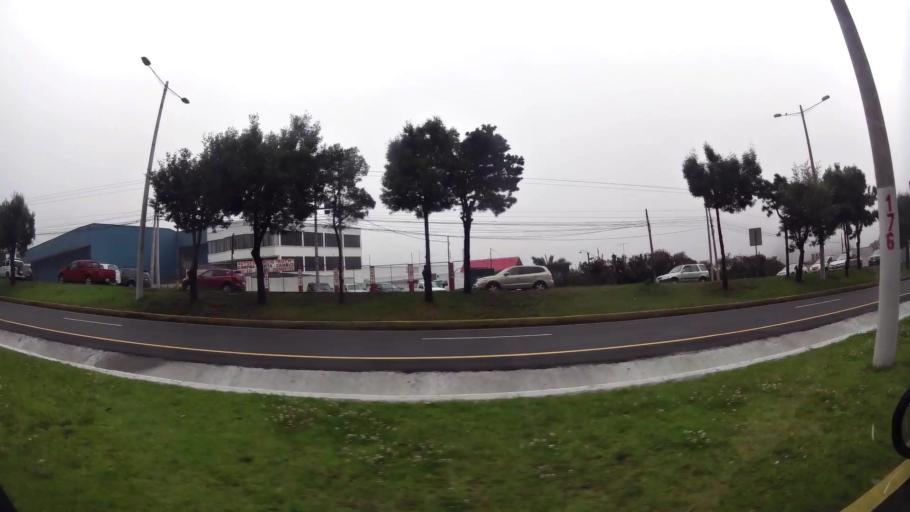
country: EC
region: Pichincha
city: Quito
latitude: -0.2620
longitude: -78.4885
